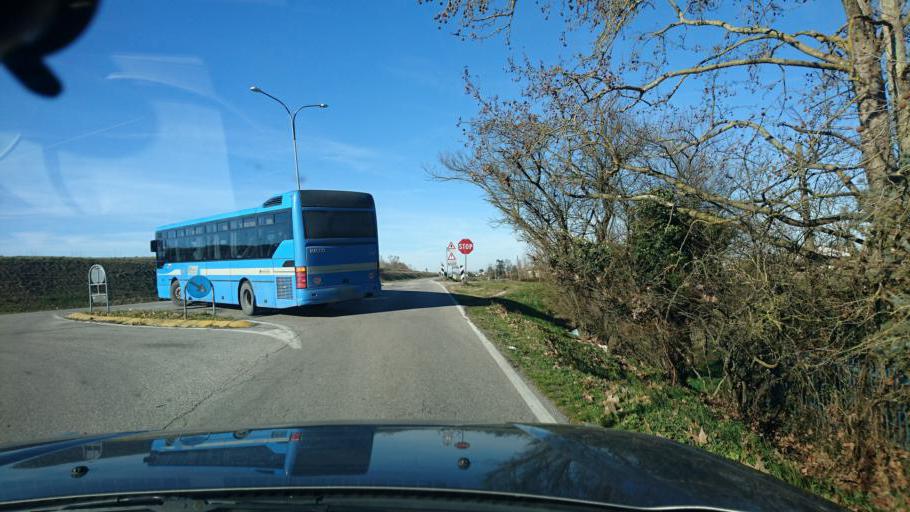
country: IT
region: Veneto
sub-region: Provincia di Rovigo
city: Ariano
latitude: 44.9521
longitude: 12.1204
